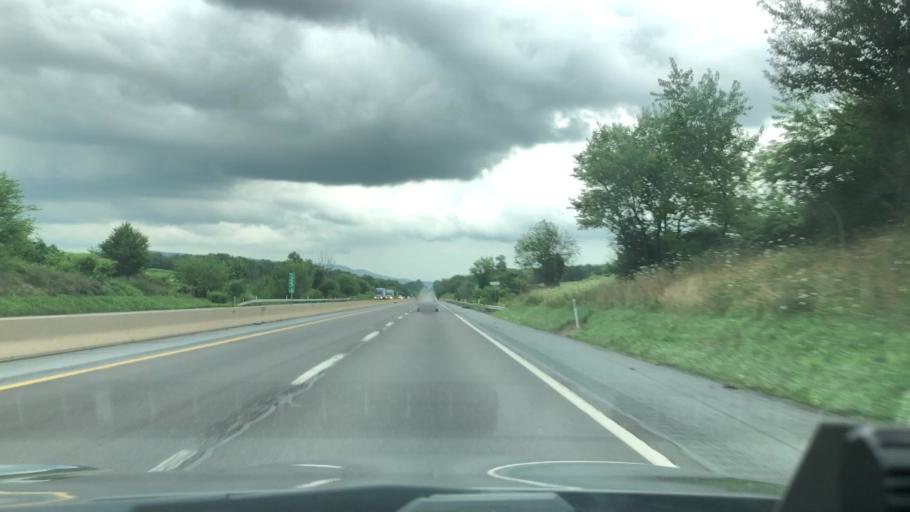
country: US
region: Pennsylvania
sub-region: Berks County
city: West Hamburg
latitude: 40.5315
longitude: -76.0661
